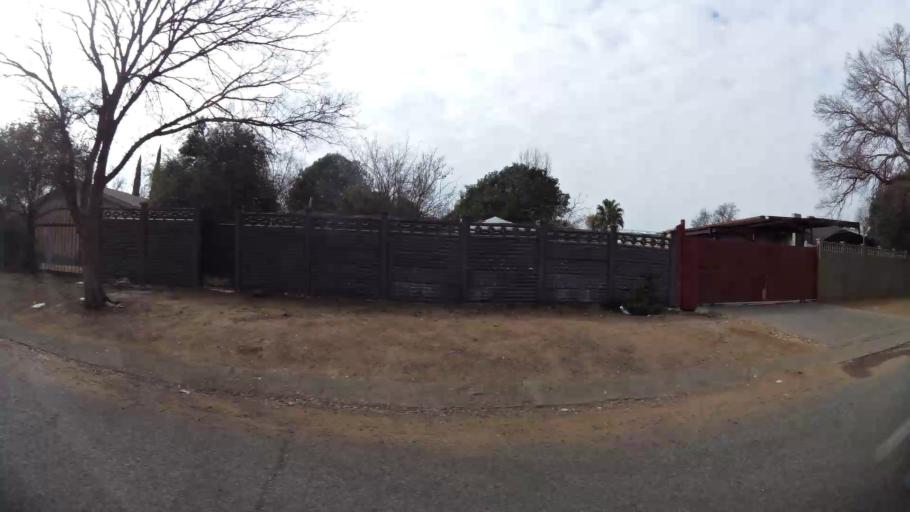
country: ZA
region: Orange Free State
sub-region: Mangaung Metropolitan Municipality
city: Bloemfontein
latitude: -29.1319
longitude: 26.1948
